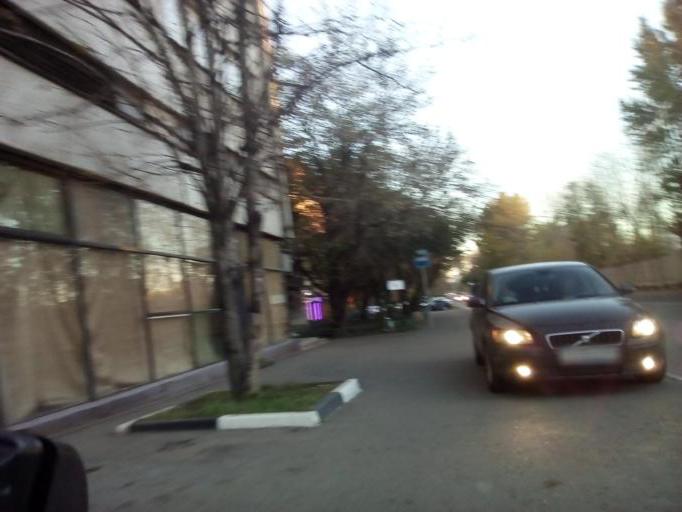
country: RU
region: Moscow
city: Sokol
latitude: 55.8052
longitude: 37.4946
